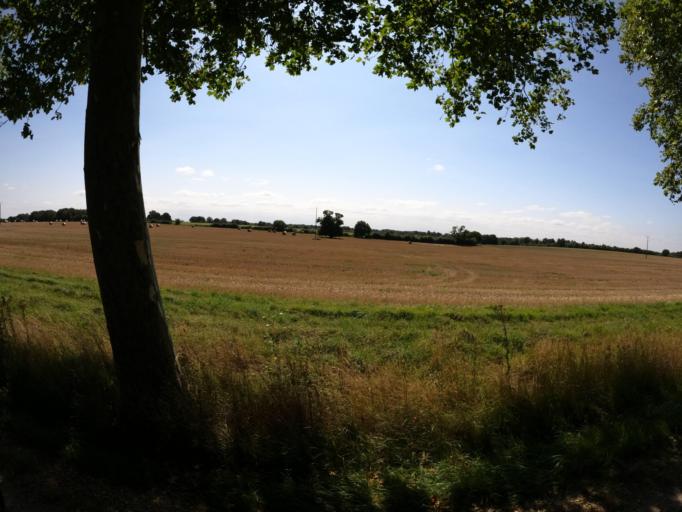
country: FR
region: Poitou-Charentes
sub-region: Departement de la Vienne
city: Charroux
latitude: 46.1371
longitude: 0.4434
